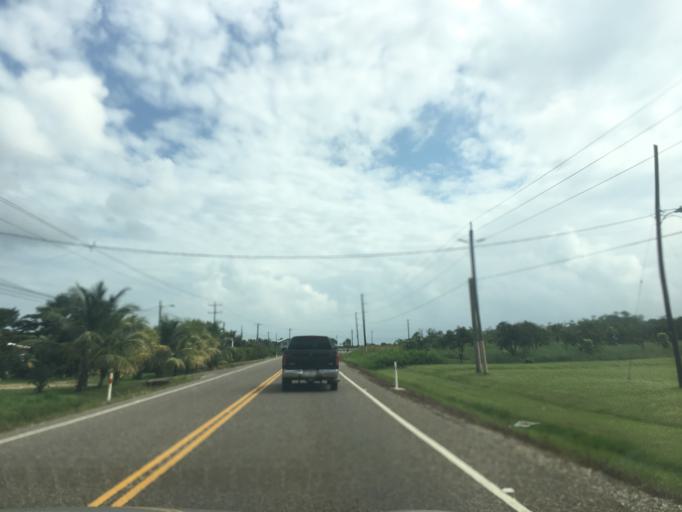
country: BZ
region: Stann Creek
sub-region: Dangriga
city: Dangriga
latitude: 17.0027
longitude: -88.3056
